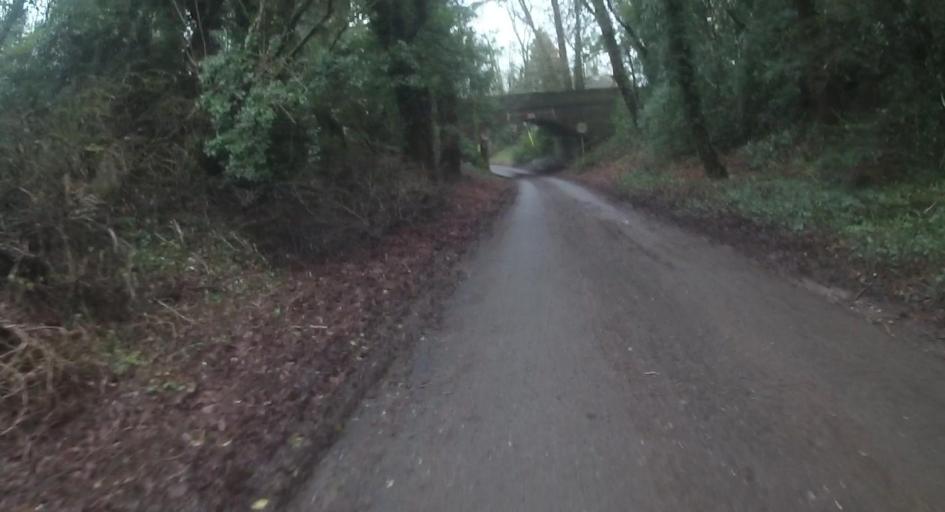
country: GB
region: England
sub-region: Hampshire
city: Kings Worthy
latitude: 51.0949
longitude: -1.2523
